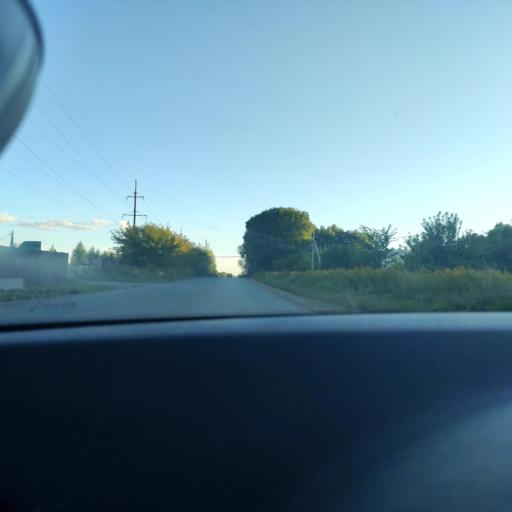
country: RU
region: Samara
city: Novosemeykino
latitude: 53.3346
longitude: 50.3192
